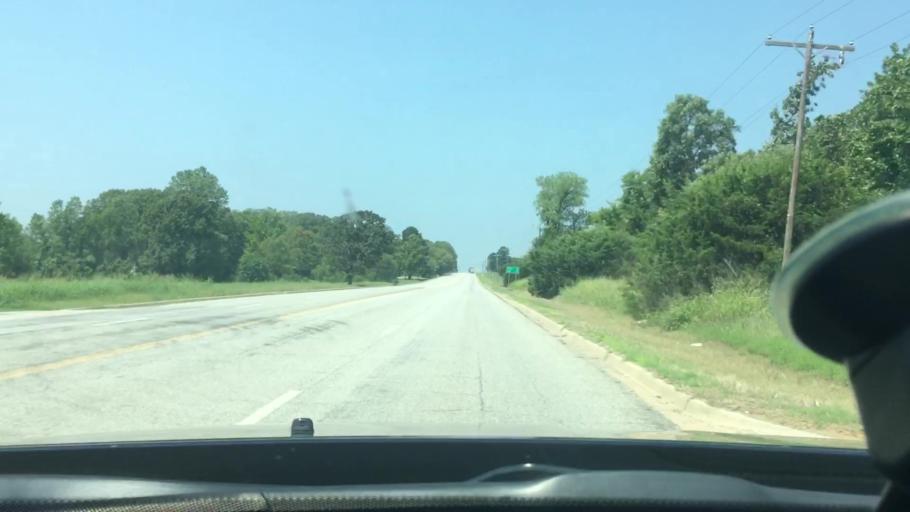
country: US
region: Oklahoma
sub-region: Atoka County
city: Atoka
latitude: 34.3025
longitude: -95.9972
